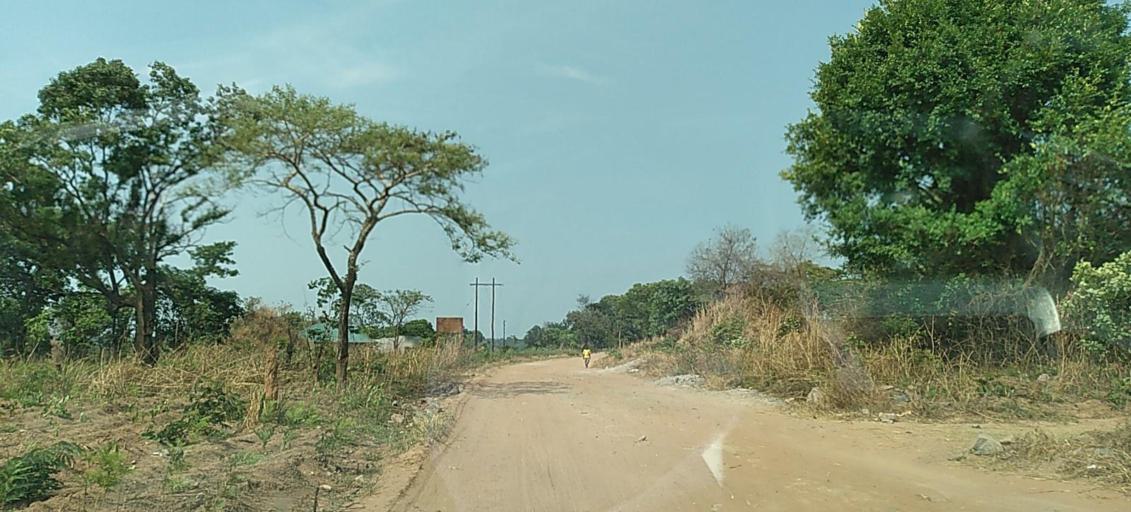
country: ZM
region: Copperbelt
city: Chililabombwe
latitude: -12.3355
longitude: 27.7275
